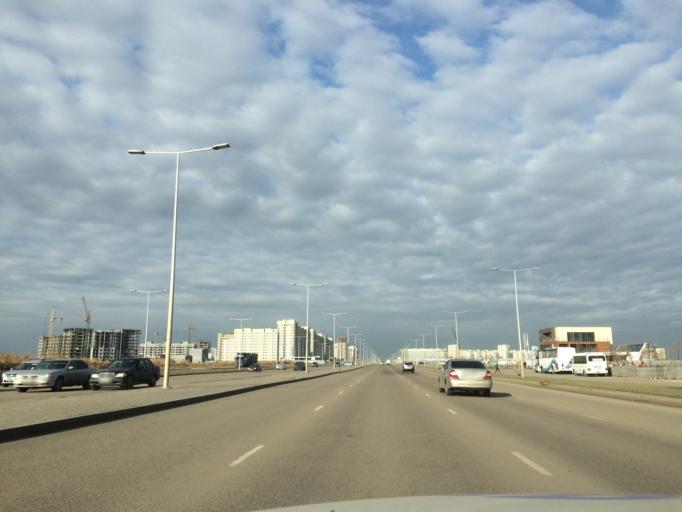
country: KZ
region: Astana Qalasy
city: Astana
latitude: 51.1288
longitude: 71.3913
